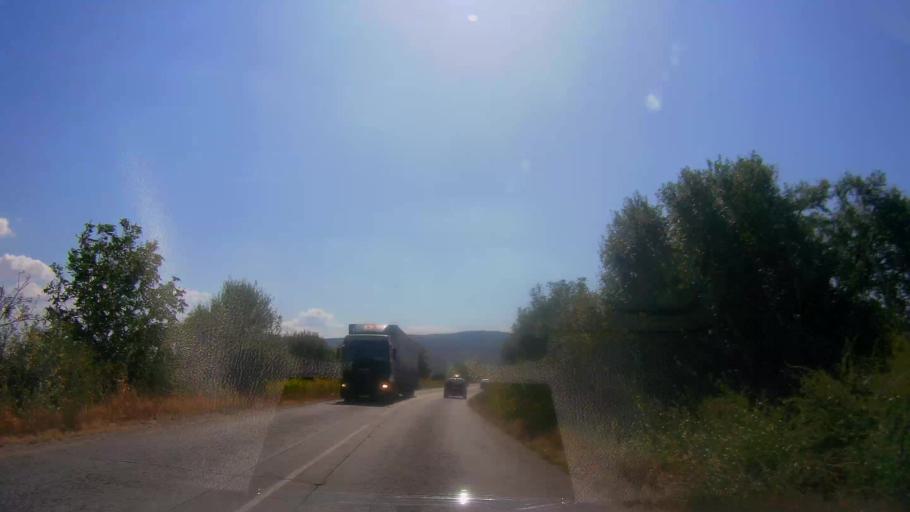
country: BG
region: Veliko Turnovo
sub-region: Obshtina Gorna Oryakhovitsa
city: Purvomaytsi
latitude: 43.1624
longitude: 25.6192
